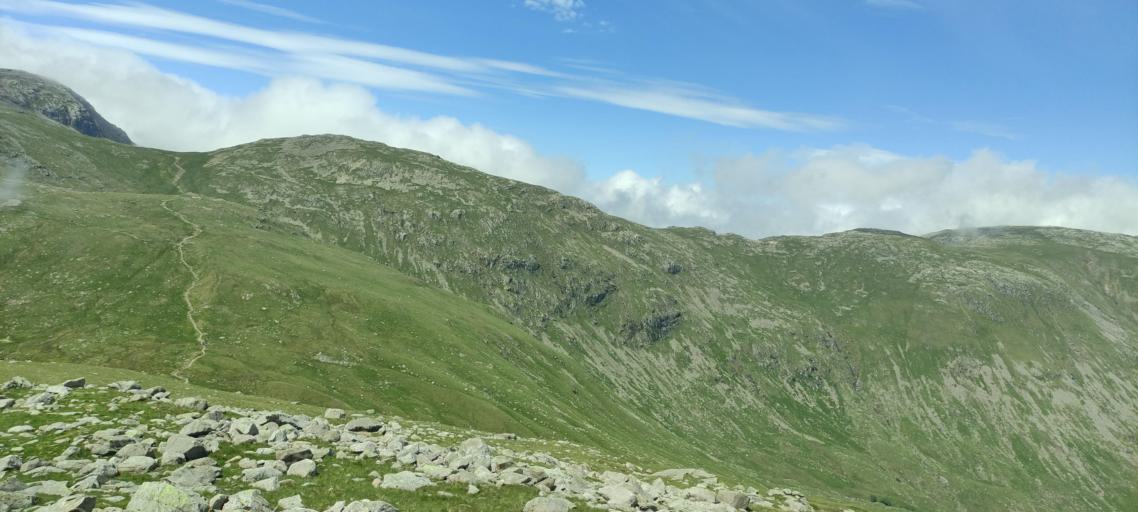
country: GB
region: England
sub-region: Cumbria
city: Keswick
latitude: 54.4579
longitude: -3.1598
